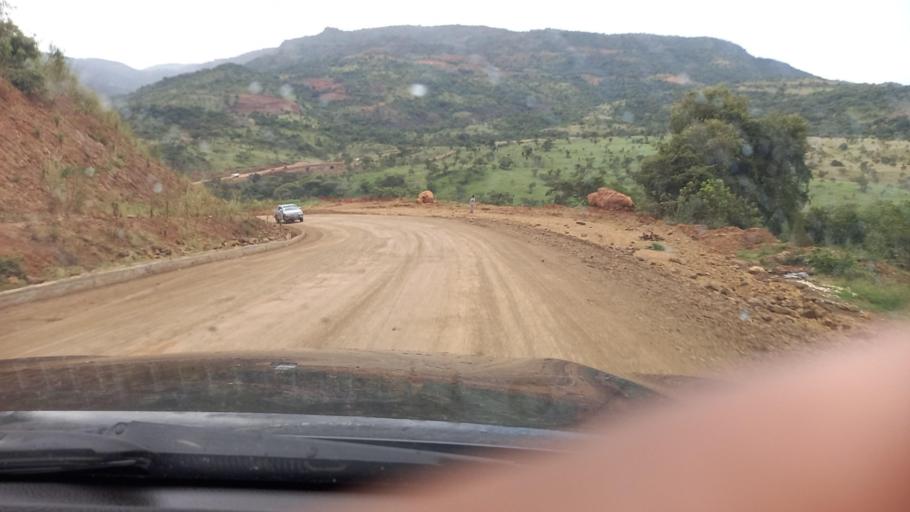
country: ET
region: Southern Nations, Nationalities, and People's Region
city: Mizan Teferi
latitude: 6.1911
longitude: 35.6798
